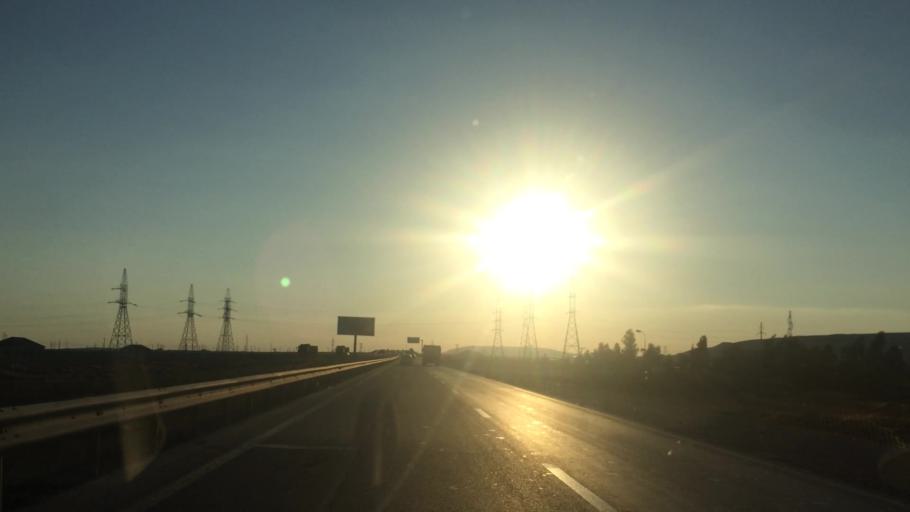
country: AZ
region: Baki
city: Qobustan
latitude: 39.9636
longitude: 49.4008
